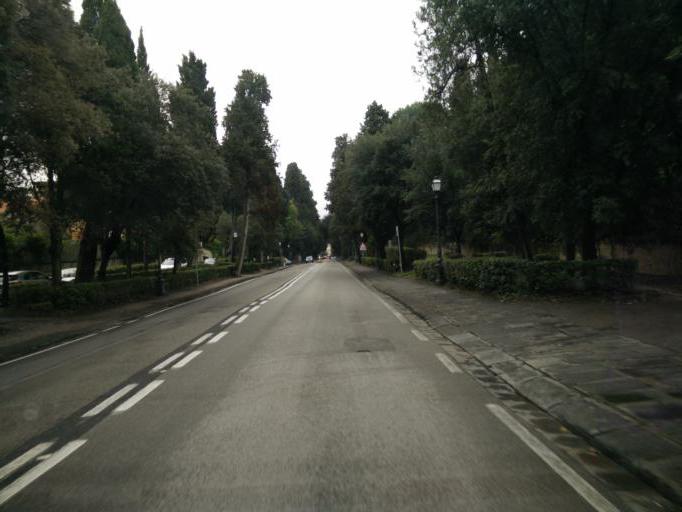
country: IT
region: Tuscany
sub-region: Province of Florence
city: Florence
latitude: 43.7569
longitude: 11.2436
